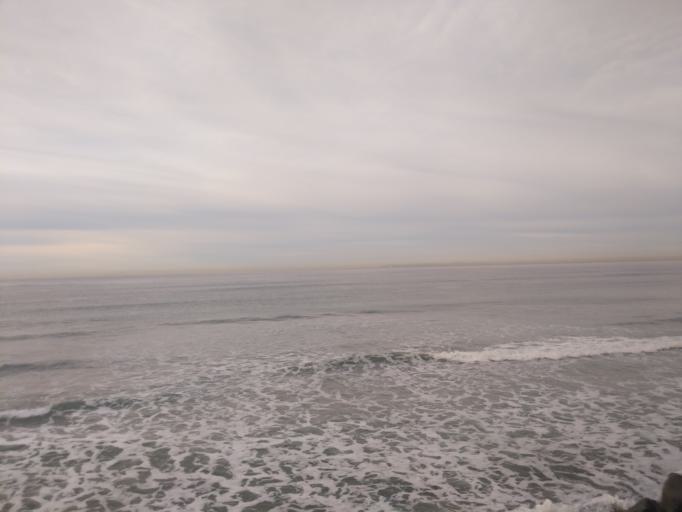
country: US
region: California
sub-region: Orange County
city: San Clemente
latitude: 33.4259
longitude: -117.6272
